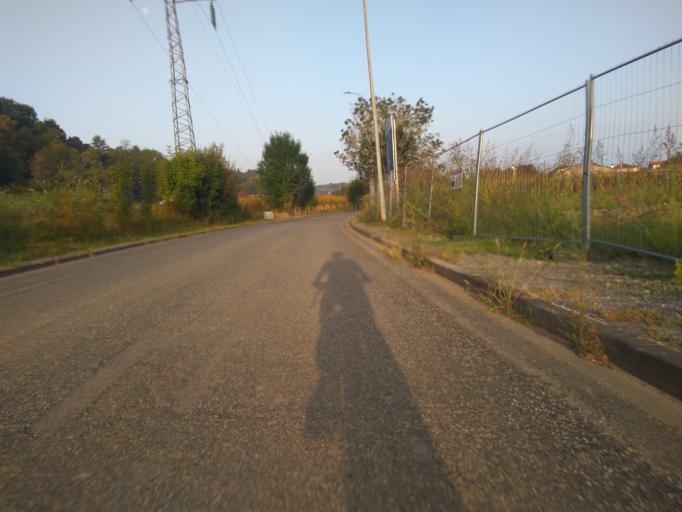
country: FR
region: Aquitaine
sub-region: Departement des Pyrenees-Atlantiques
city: Gelos
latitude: 43.2792
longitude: -0.3686
